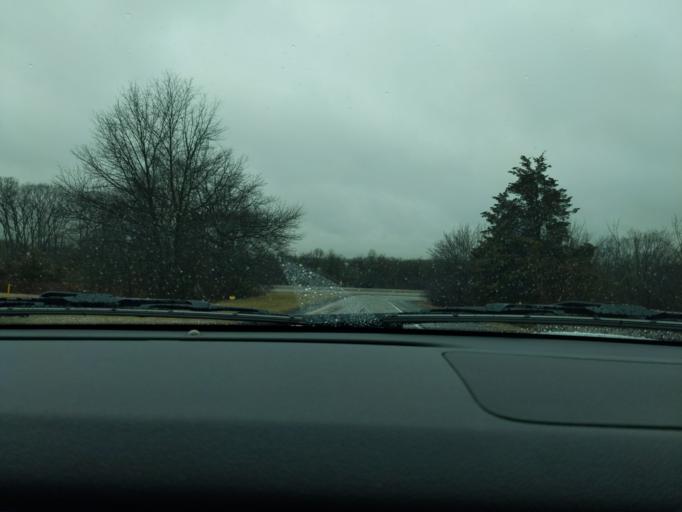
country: US
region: Pennsylvania
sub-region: Bucks County
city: Doylestown
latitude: 40.3049
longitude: -75.1476
